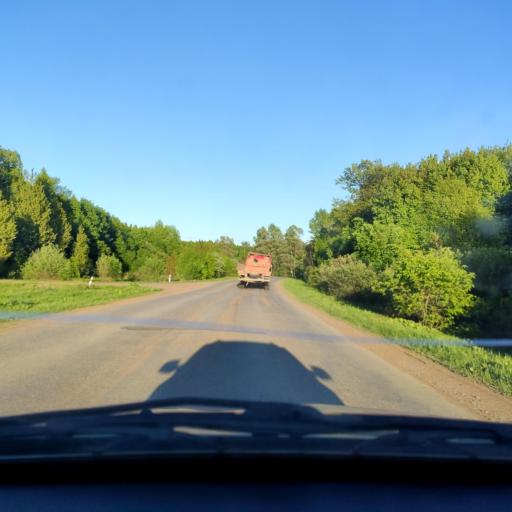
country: RU
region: Bashkortostan
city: Blagoveshchensk
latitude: 55.0317
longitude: 56.1045
